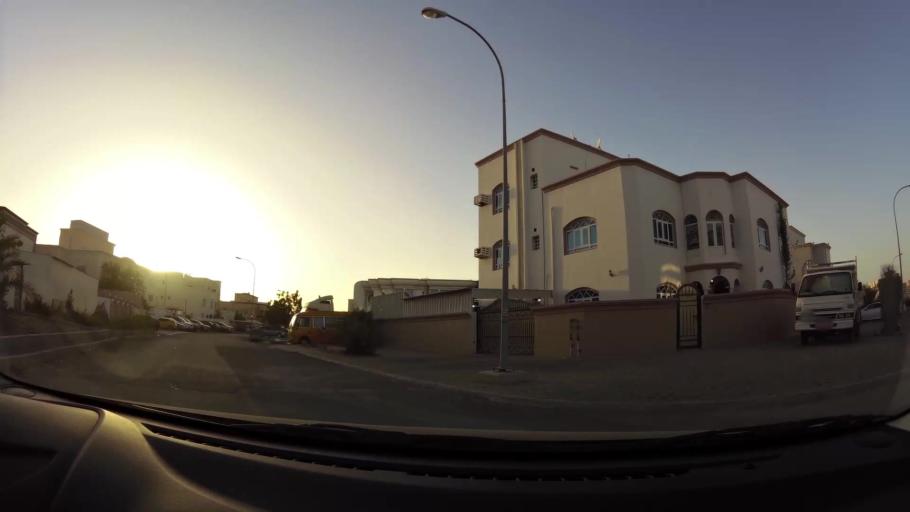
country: OM
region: Muhafazat Masqat
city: As Sib al Jadidah
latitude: 23.6052
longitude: 58.2295
